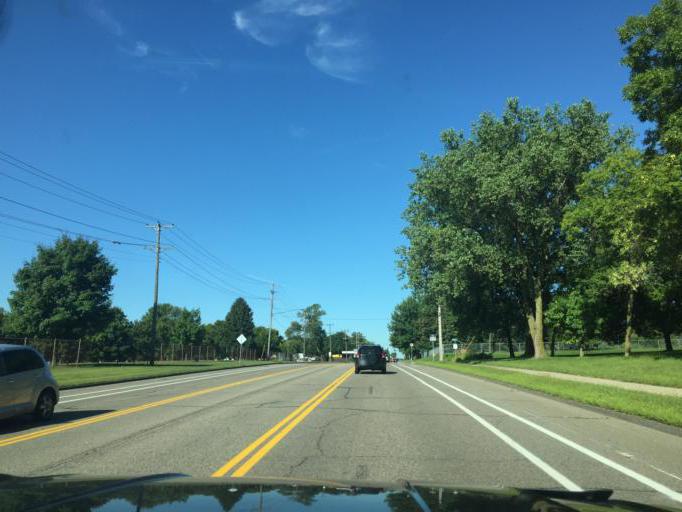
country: US
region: Minnesota
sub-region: Ramsey County
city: Roseville
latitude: 44.9918
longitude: -93.1223
